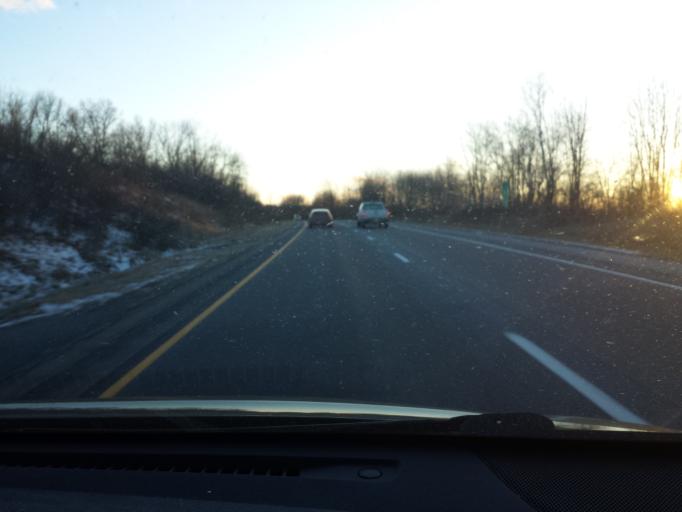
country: US
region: Pennsylvania
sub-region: Centre County
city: Zion
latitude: 40.9963
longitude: -77.6120
